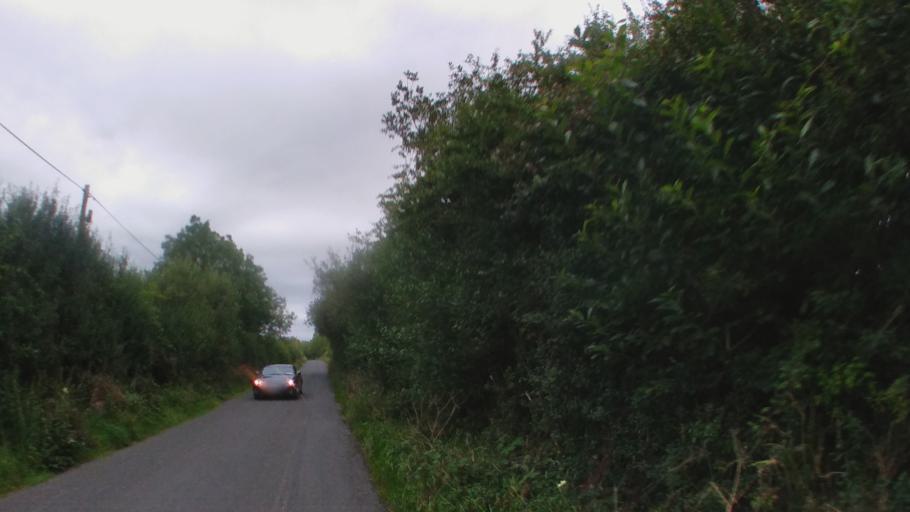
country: IE
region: Leinster
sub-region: Kilkenny
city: Kilkenny
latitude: 52.6828
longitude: -7.2207
